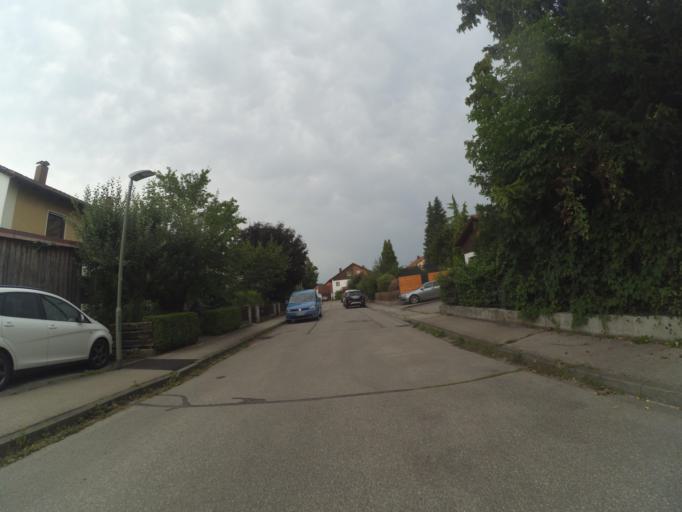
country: DE
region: Bavaria
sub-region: Swabia
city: Buchloe
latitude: 48.0365
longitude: 10.7114
